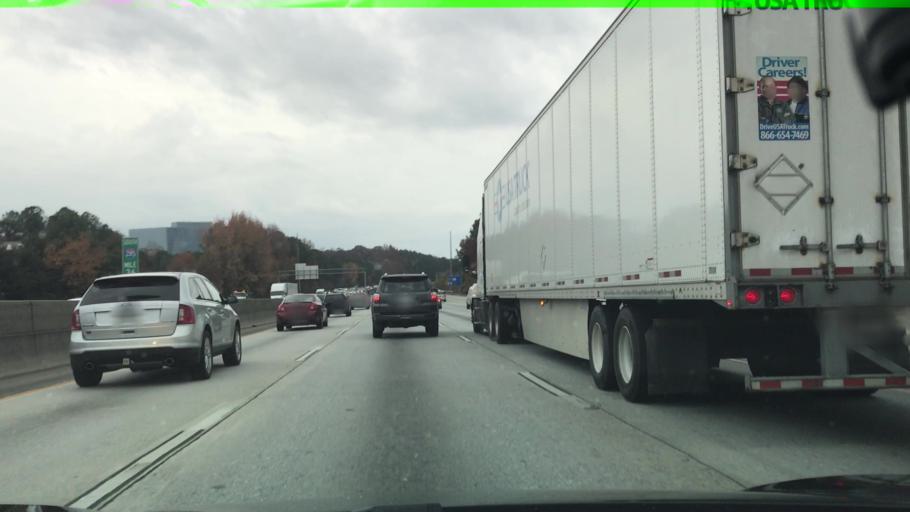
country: US
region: Georgia
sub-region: DeKalb County
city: Tucker
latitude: 33.8436
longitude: -84.2477
